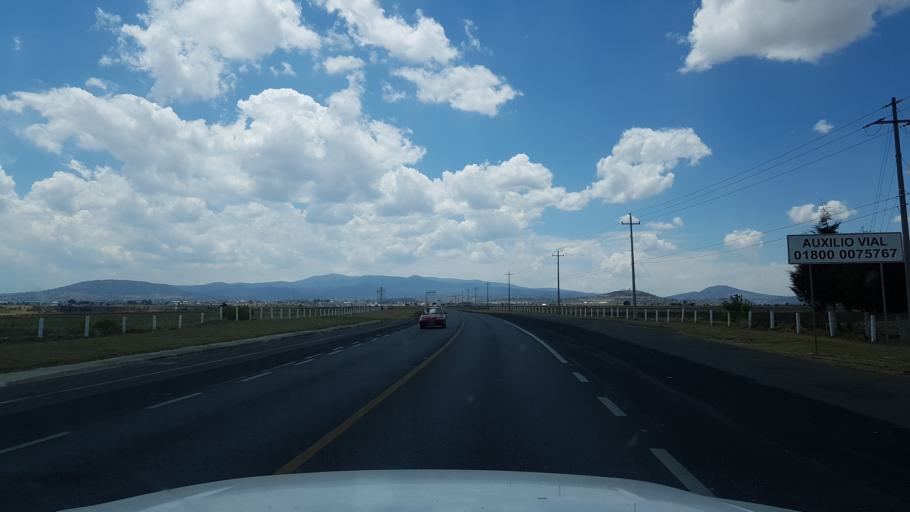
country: MX
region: Hidalgo
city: Calpulalpan
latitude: 19.6170
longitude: -98.5525
